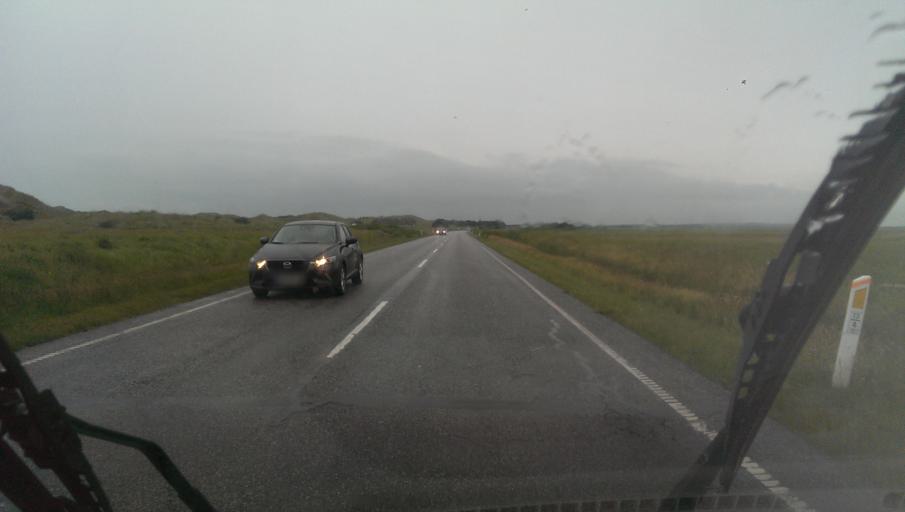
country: DK
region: Central Jutland
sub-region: Ringkobing-Skjern Kommune
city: Ringkobing
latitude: 56.2351
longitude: 8.1390
